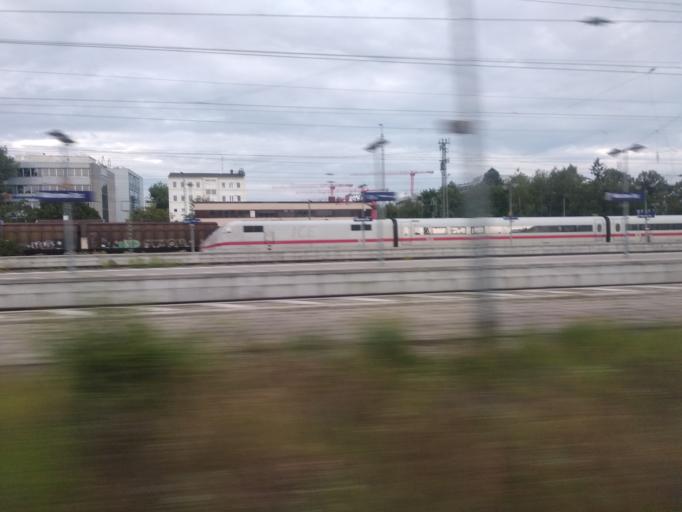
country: DE
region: Bavaria
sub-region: Upper Bavaria
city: Bogenhausen
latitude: 48.1289
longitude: 11.6076
